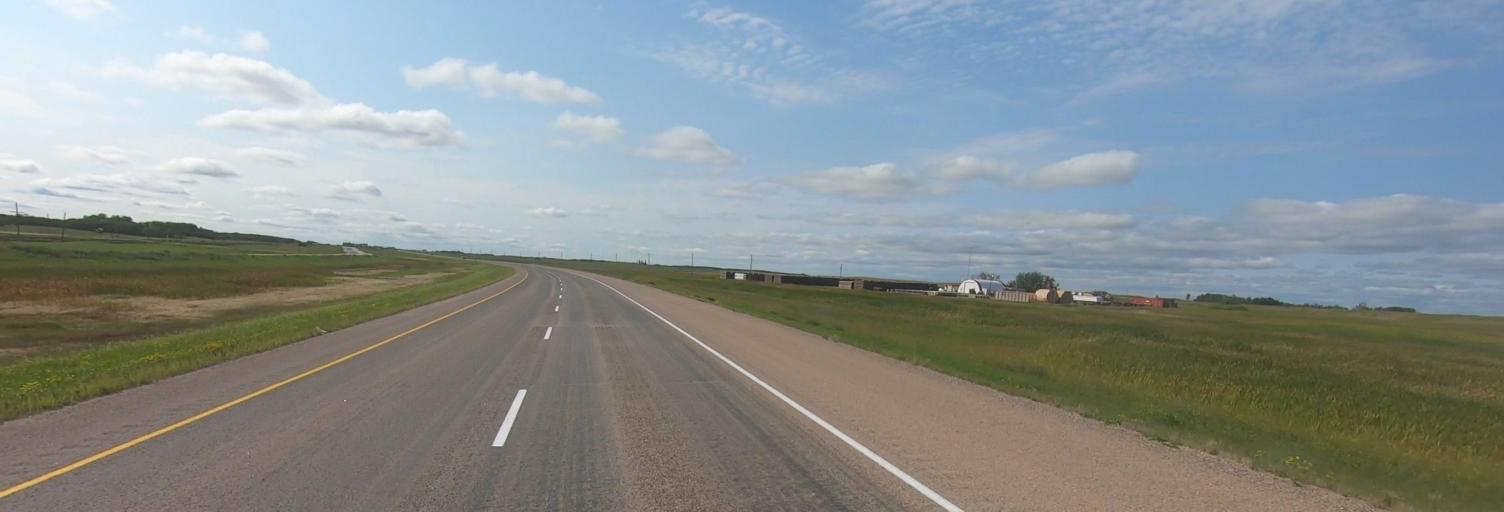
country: CA
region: Saskatchewan
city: Moosomin
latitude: 50.0084
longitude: -101.3063
